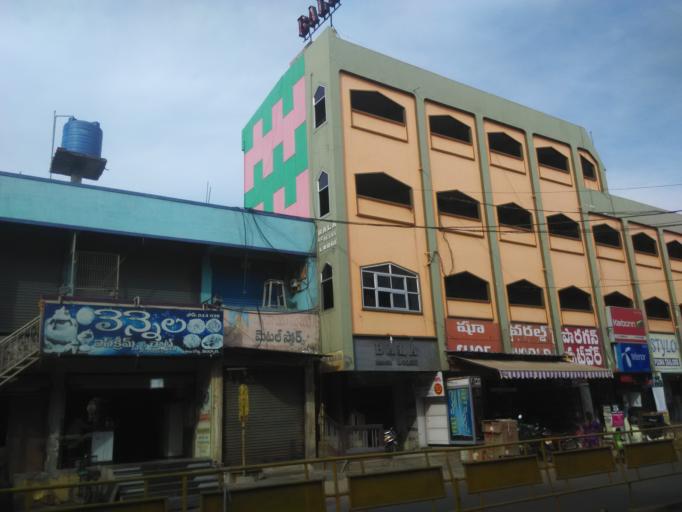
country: IN
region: Andhra Pradesh
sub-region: Kurnool
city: Nandyal
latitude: 15.4853
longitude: 78.4860
